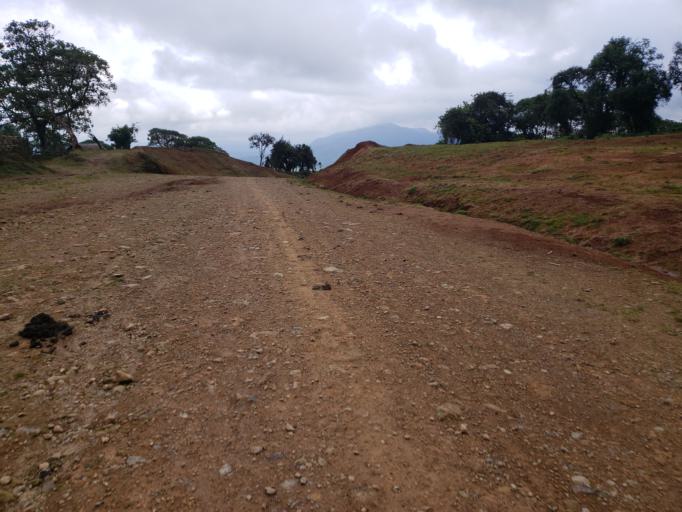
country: ET
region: Oromiya
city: Dodola
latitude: 6.6891
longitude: 39.3699
